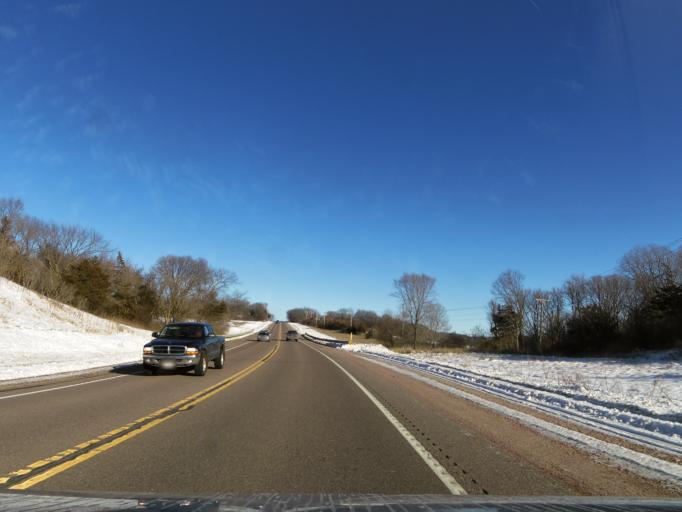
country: US
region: Wisconsin
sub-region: Sauk County
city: Baraboo
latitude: 43.4744
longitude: -89.6561
